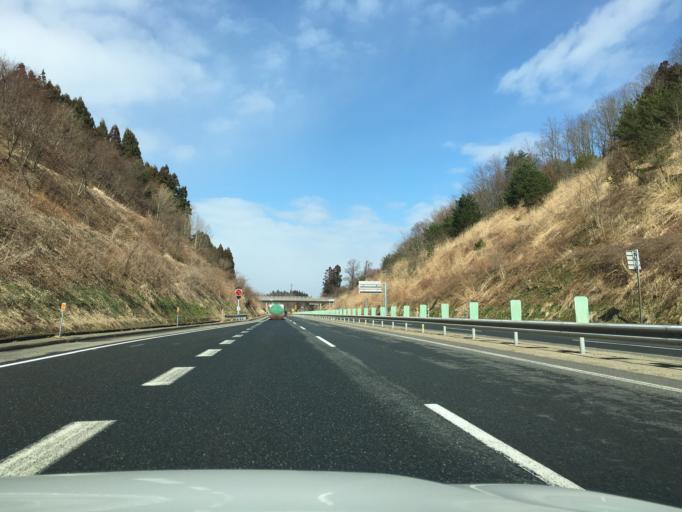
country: JP
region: Akita
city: Akita Shi
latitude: 39.7836
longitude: 140.1105
